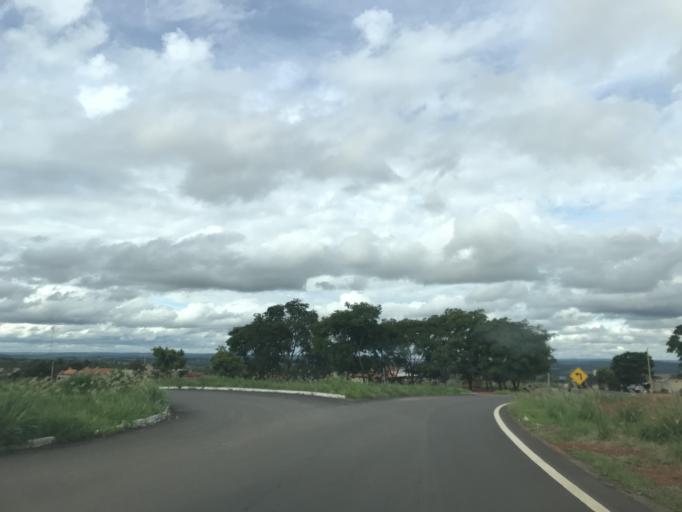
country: BR
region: Goias
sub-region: Piracanjuba
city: Piracanjuba
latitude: -17.2085
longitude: -48.7079
